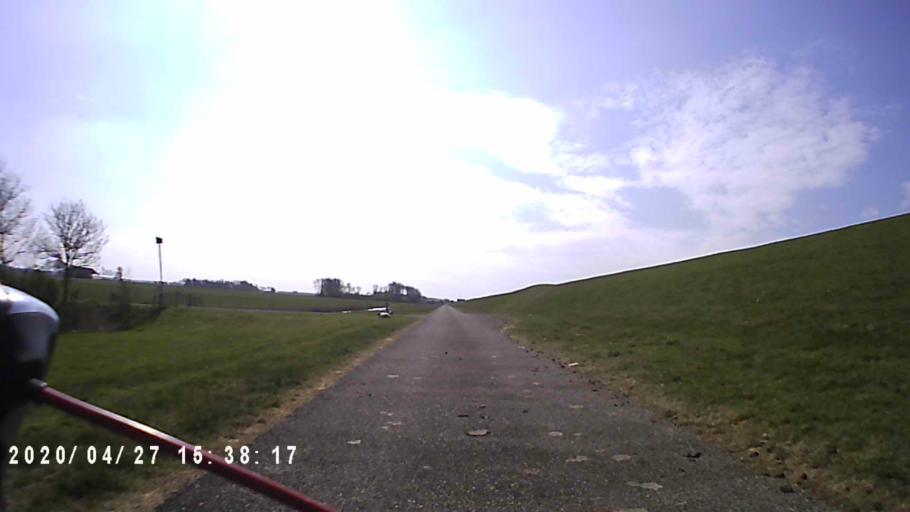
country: NL
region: Groningen
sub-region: Gemeente De Marne
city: Ulrum
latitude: 53.3947
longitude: 6.3183
